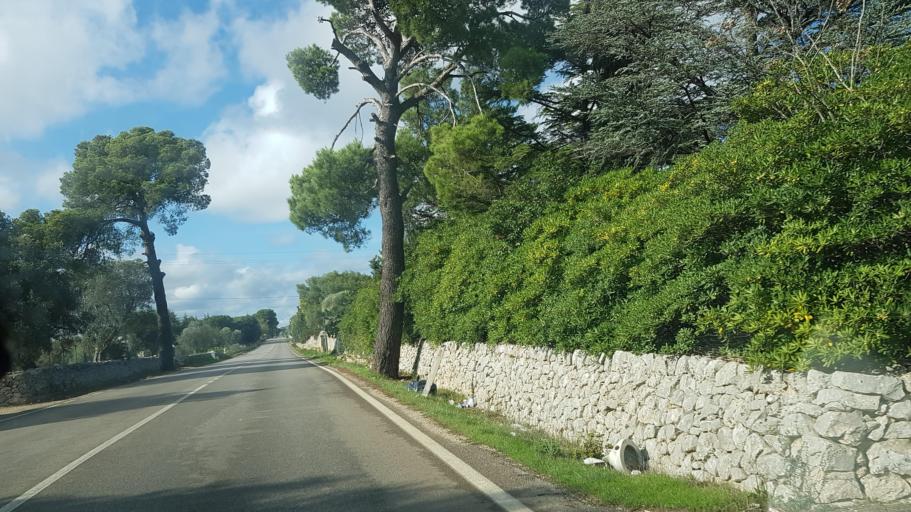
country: IT
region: Apulia
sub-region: Provincia di Brindisi
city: Carovigno
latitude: 40.7090
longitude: 17.6414
